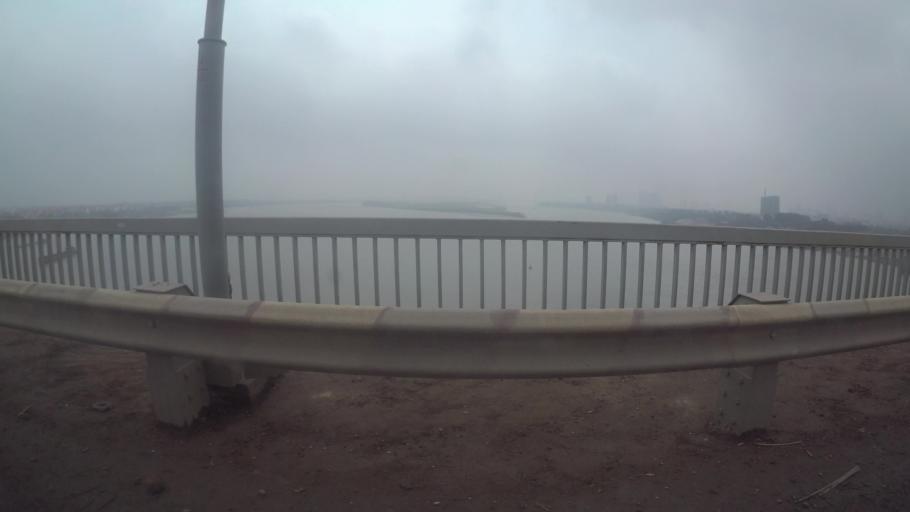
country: VN
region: Ha Noi
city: Tay Ho
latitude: 21.0978
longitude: 105.7865
